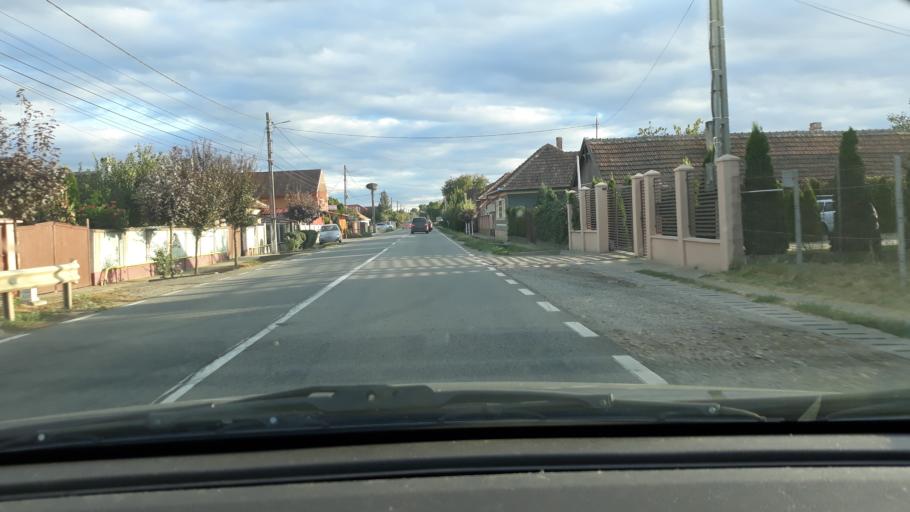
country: RO
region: Bihor
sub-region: Comuna Biharea
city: Biharea
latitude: 47.1660
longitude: 21.9221
